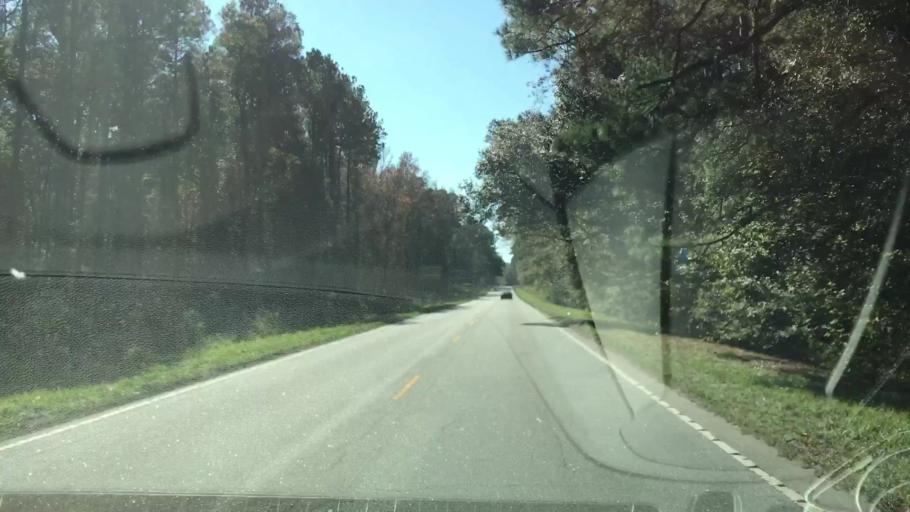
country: US
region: South Carolina
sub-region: Jasper County
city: Ridgeland
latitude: 32.3994
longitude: -80.9066
